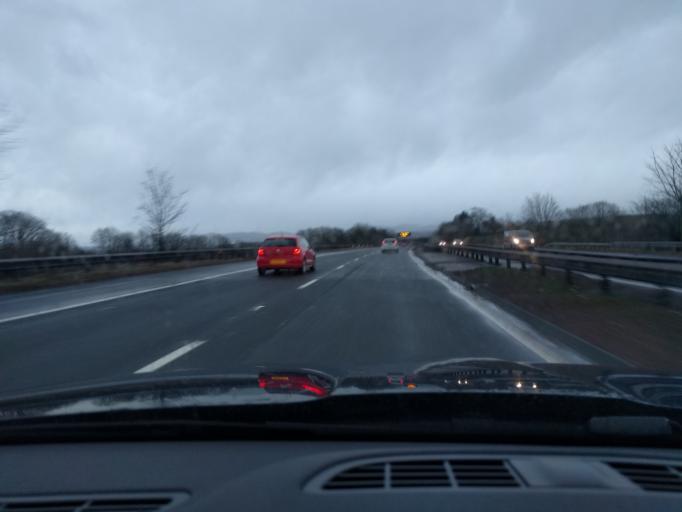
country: GB
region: Scotland
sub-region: West Lothian
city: Broxburn
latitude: 55.9651
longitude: -3.4465
